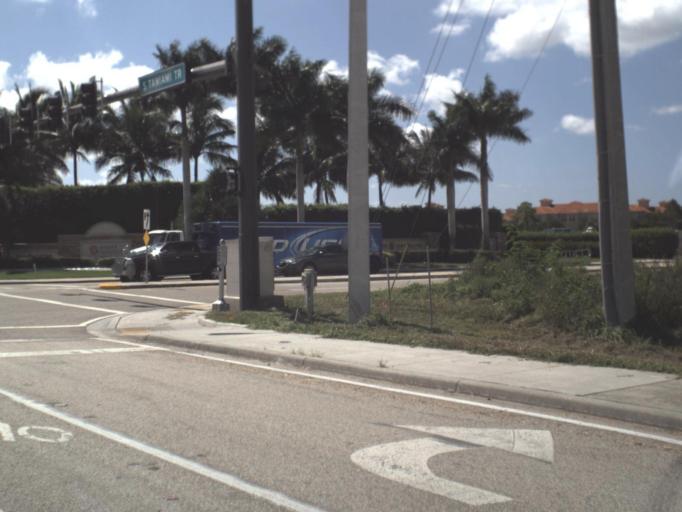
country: US
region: Florida
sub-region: Lee County
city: Estero
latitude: 26.3983
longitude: -81.8108
